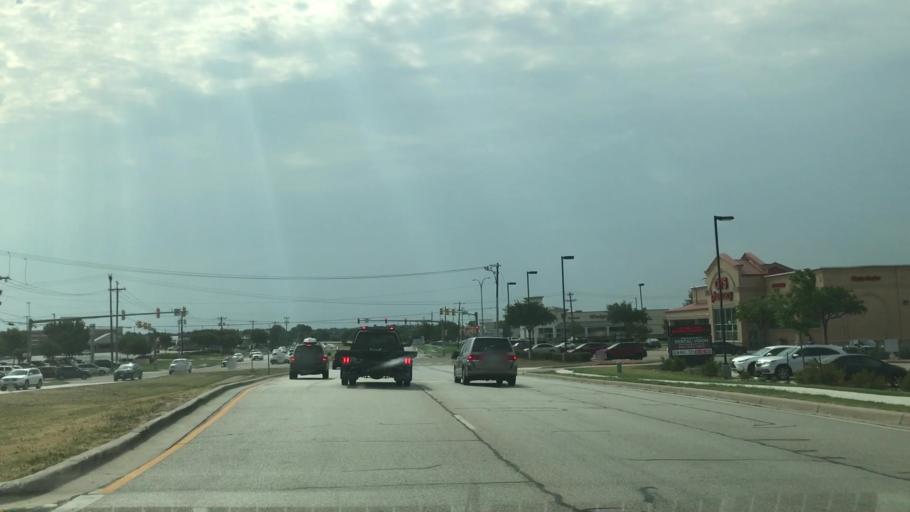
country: US
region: Texas
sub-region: Tarrant County
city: Watauga
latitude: 32.8944
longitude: -97.2910
